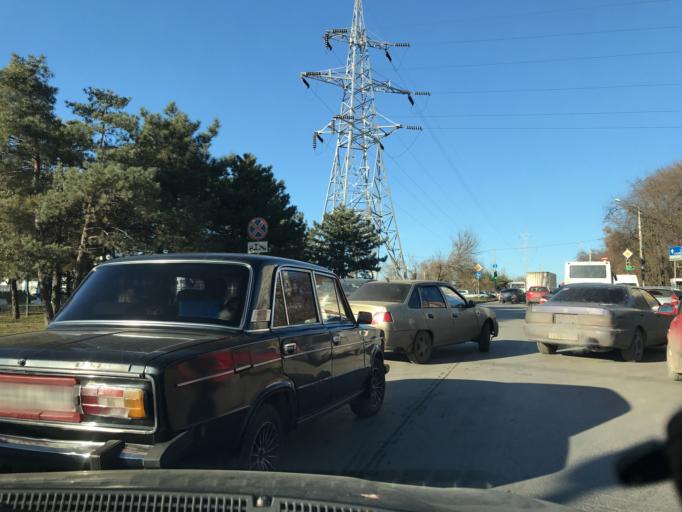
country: RU
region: Rostov
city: Kalinin
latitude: 47.2315
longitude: 39.6140
